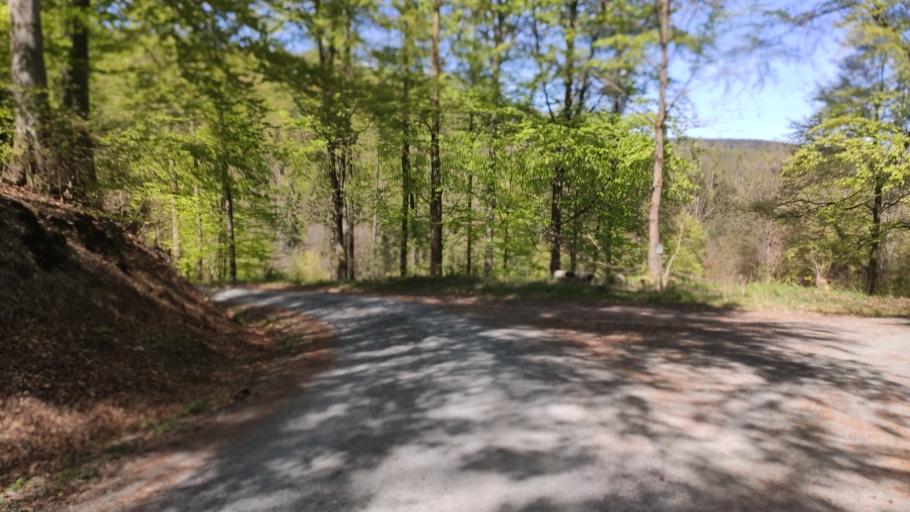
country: DE
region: Bavaria
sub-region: Upper Franconia
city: Nordhalben
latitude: 50.3602
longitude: 11.4782
